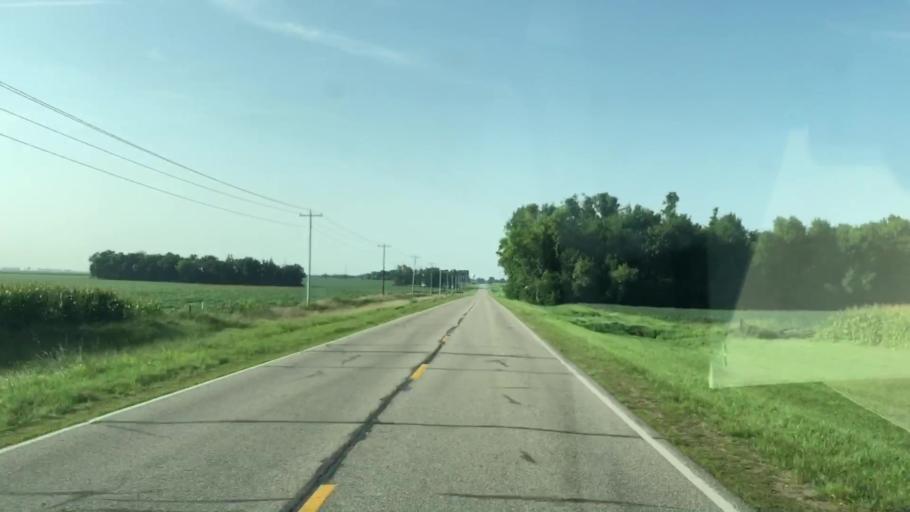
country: US
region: Iowa
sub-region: Lyon County
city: George
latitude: 43.3679
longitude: -95.9982
